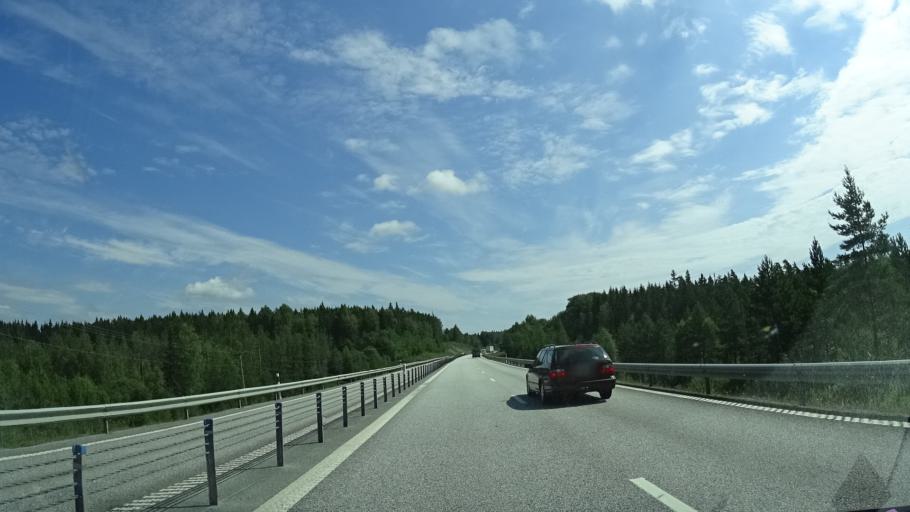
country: SE
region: OErebro
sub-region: Degerfors Kommun
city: Degerfors
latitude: 59.3241
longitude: 14.3726
